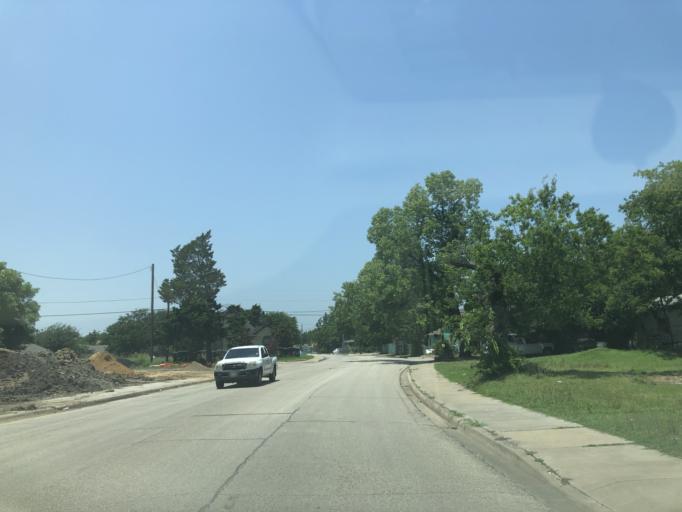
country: US
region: Texas
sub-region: Dallas County
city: Dallas
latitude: 32.7815
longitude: -96.8414
